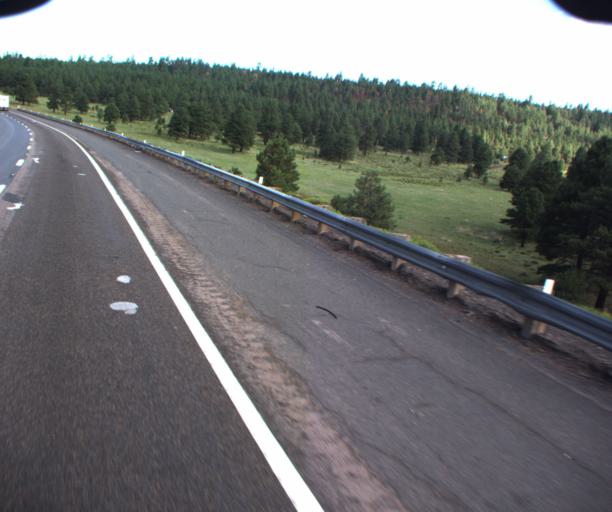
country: US
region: Arizona
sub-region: Coconino County
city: Flagstaff
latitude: 35.2118
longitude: -111.7738
